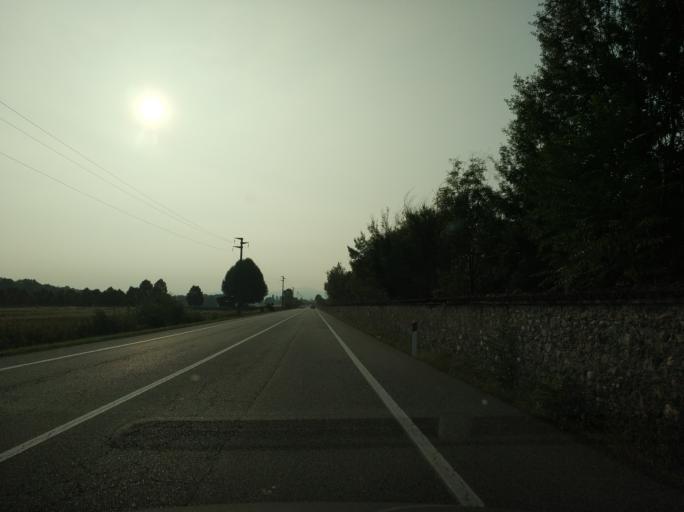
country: IT
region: Piedmont
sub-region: Provincia di Torino
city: Druento
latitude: 45.1626
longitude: 7.6008
